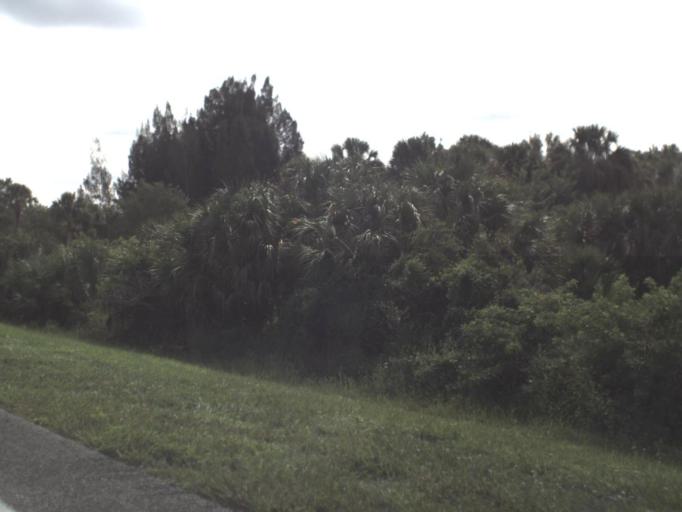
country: US
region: Florida
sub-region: Lee County
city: Olga
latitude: 26.7152
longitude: -81.6753
